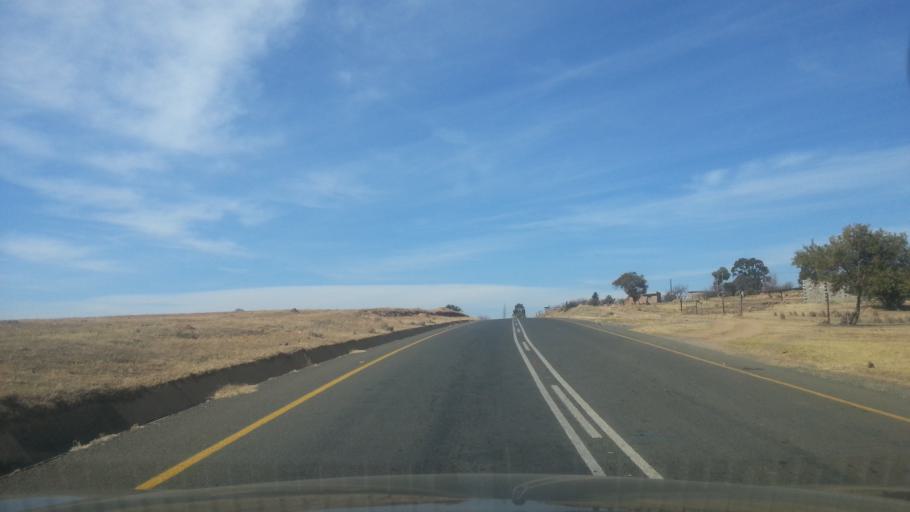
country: LS
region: Maseru
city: Maseru
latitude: -29.4921
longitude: 27.5361
